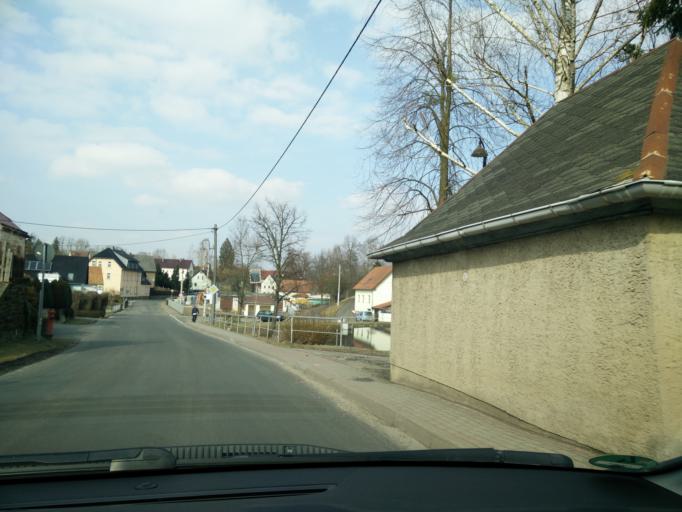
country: DE
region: Saxony
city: Colditz
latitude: 51.1168
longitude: 12.7864
